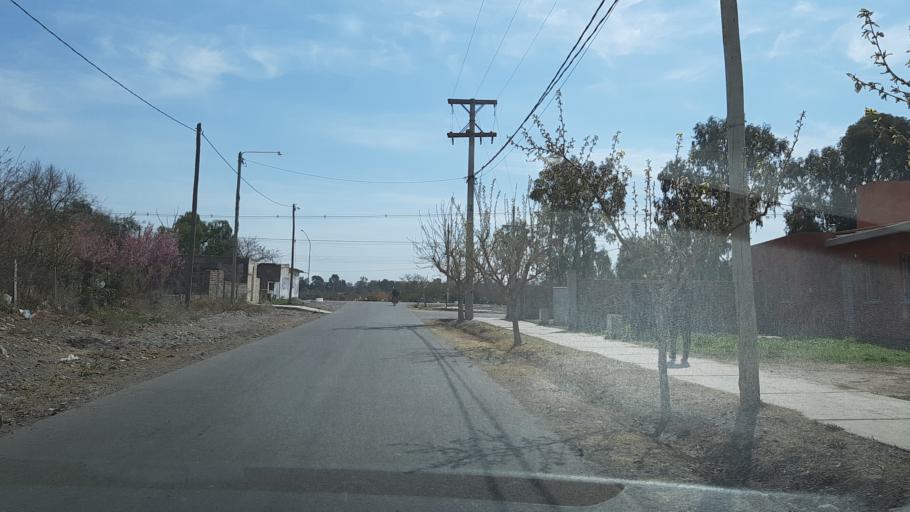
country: AR
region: San Juan
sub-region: Departamento de Zonda
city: Zonda
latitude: -31.5447
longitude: -68.7418
